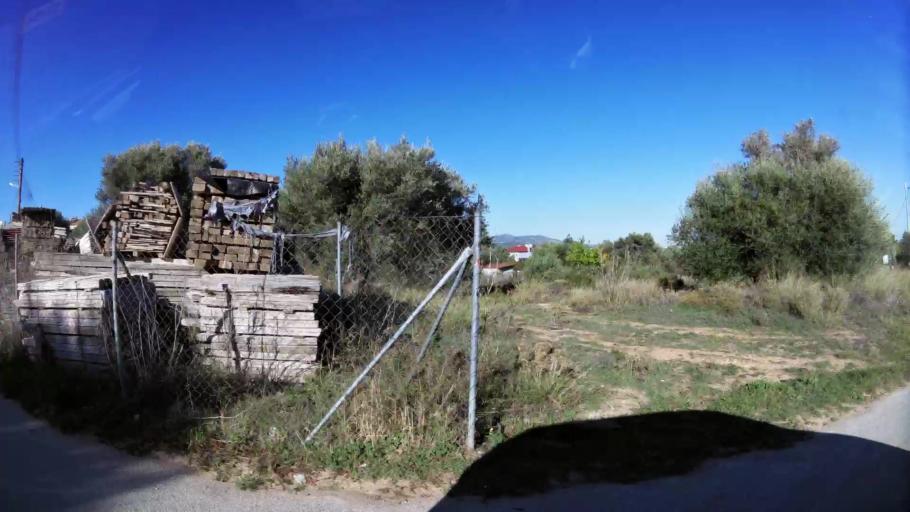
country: GR
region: Attica
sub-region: Nomarchia Anatolikis Attikis
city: Leondarion
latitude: 37.9764
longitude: 23.8481
